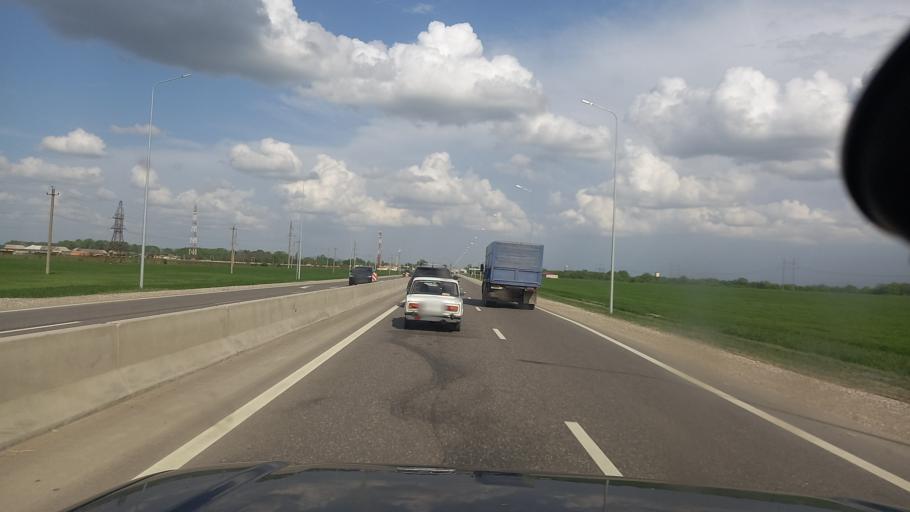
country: RU
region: Chechnya
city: Alkhan-Yurt
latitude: 43.2206
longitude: 45.5401
